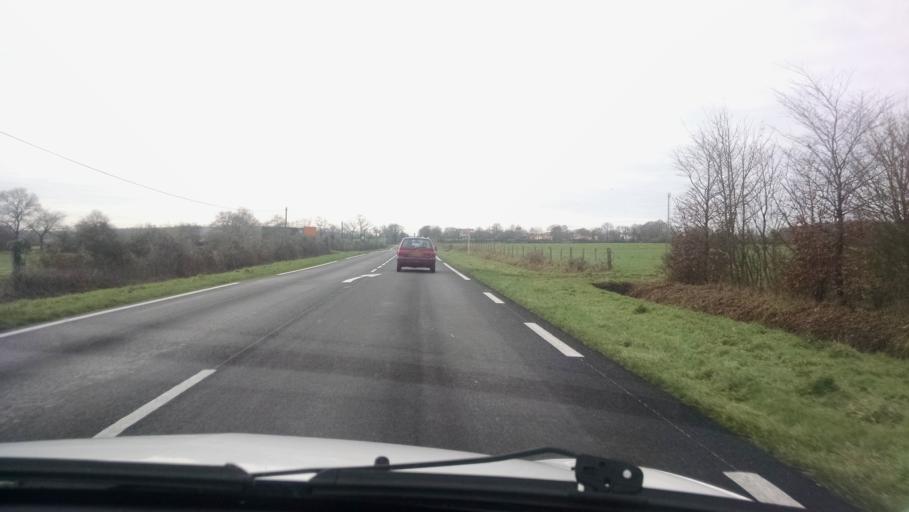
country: FR
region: Pays de la Loire
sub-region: Departement de Maine-et-Loire
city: Le Longeron
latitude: 47.0374
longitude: -1.0833
